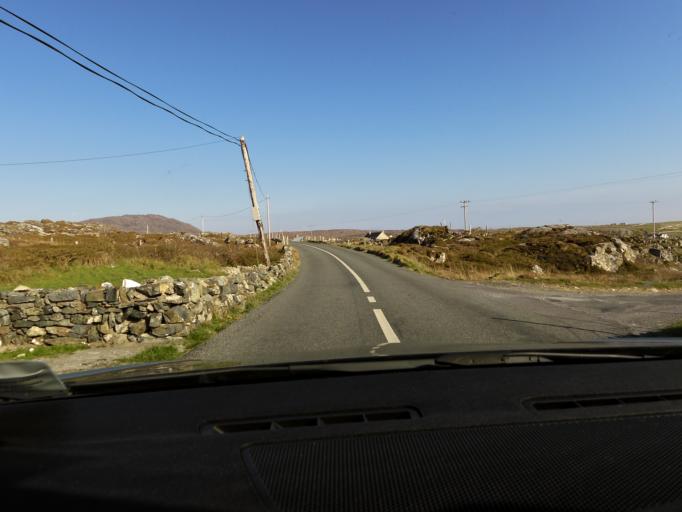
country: IE
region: Connaught
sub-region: County Galway
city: Clifden
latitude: 53.3953
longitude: -10.0186
